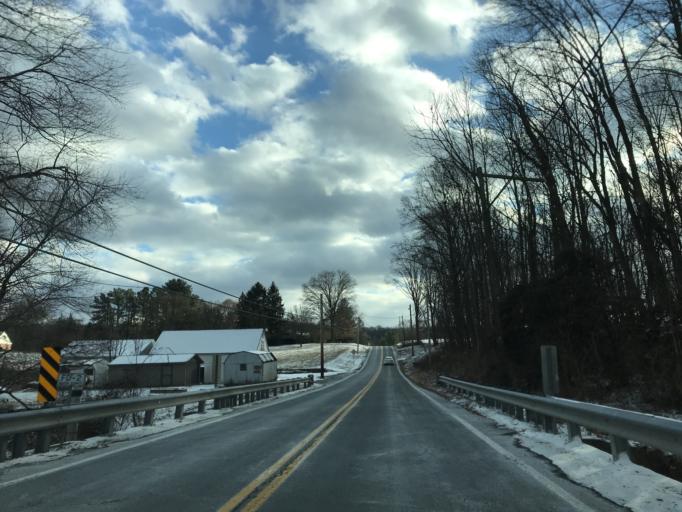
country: US
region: Maryland
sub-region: Harford County
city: Bel Air North
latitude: 39.6560
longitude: -76.3830
